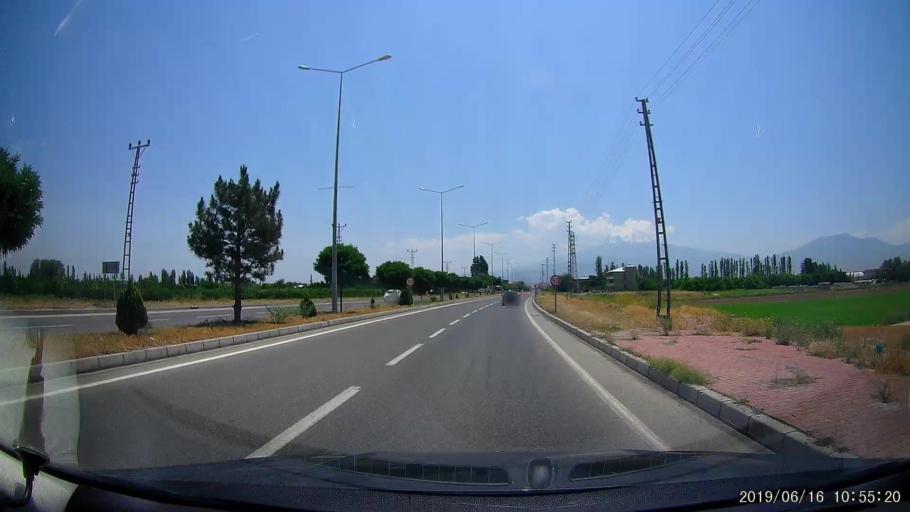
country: TR
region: Igdir
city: Igdir
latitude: 39.9367
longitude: 44.0095
